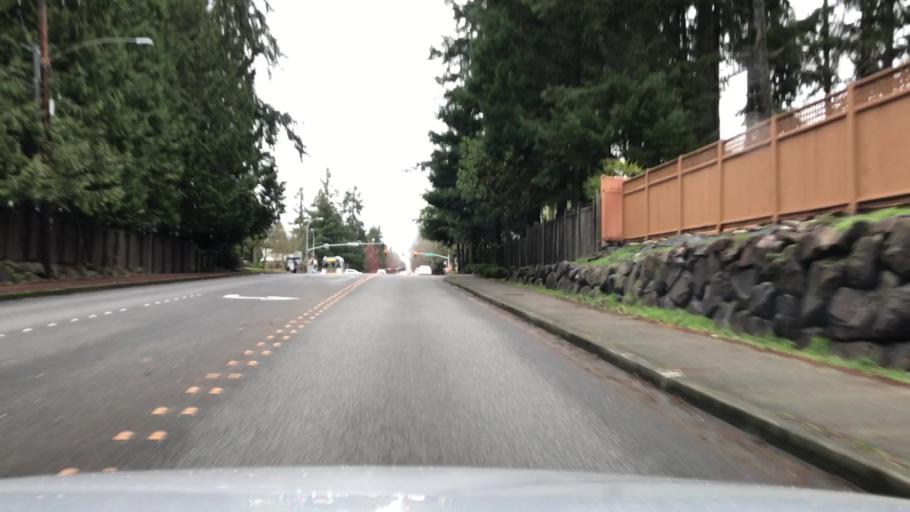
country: US
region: Washington
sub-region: King County
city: Eastgate
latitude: 47.6154
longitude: -122.1324
